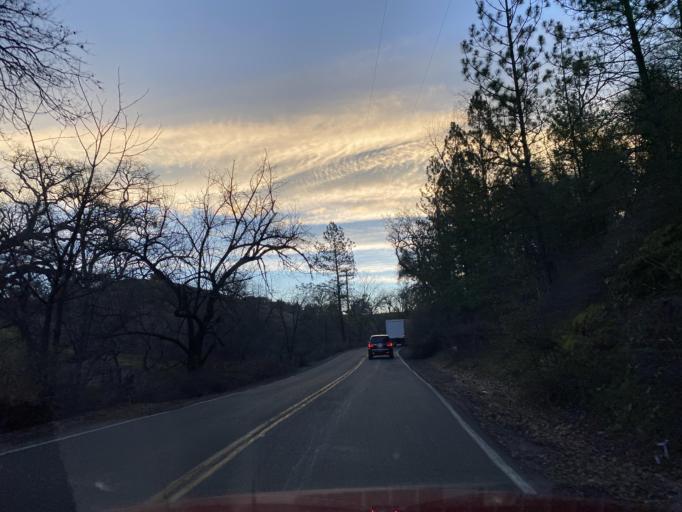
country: US
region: California
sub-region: Amador County
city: Plymouth
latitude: 38.5090
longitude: -120.7712
